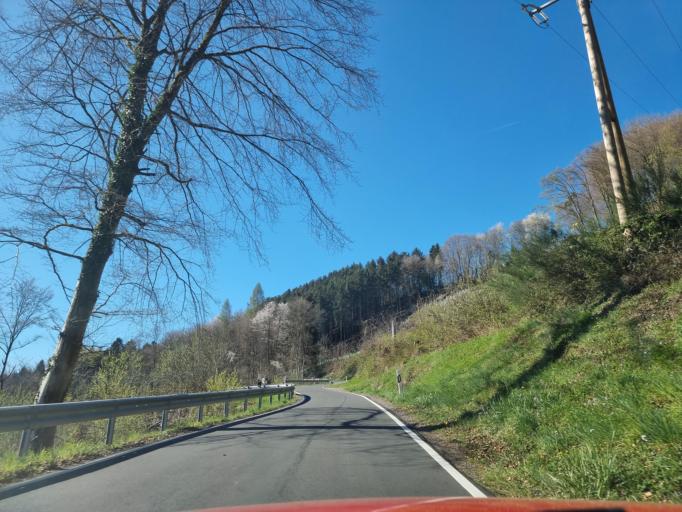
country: DE
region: Rheinland-Pfalz
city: Prumzurlay
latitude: 49.8678
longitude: 6.4308
